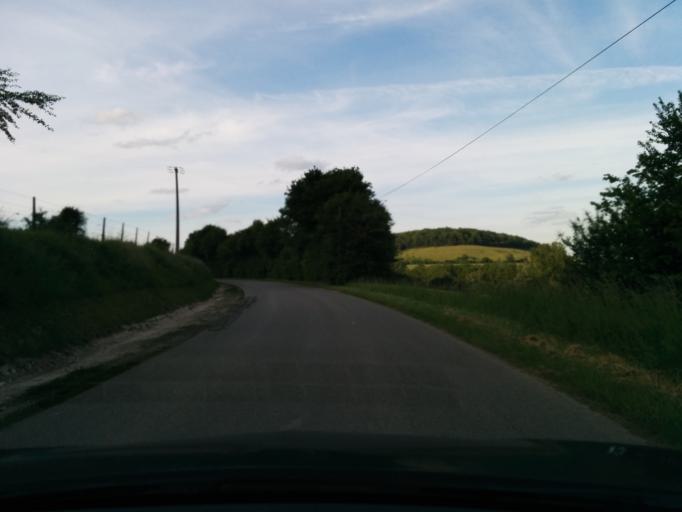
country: FR
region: Haute-Normandie
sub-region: Departement de la Seine-Maritime
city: La Feuillie
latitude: 49.5203
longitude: 1.4888
